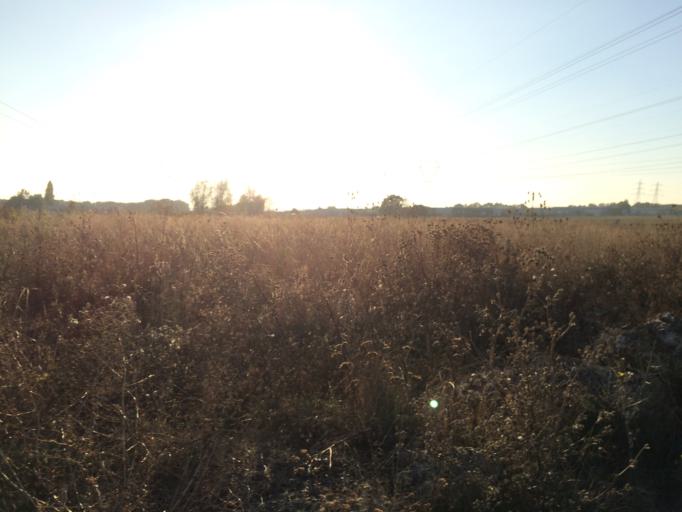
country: FR
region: Ile-de-France
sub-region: Departement de l'Essonne
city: Nozay
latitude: 48.6654
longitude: 2.2181
